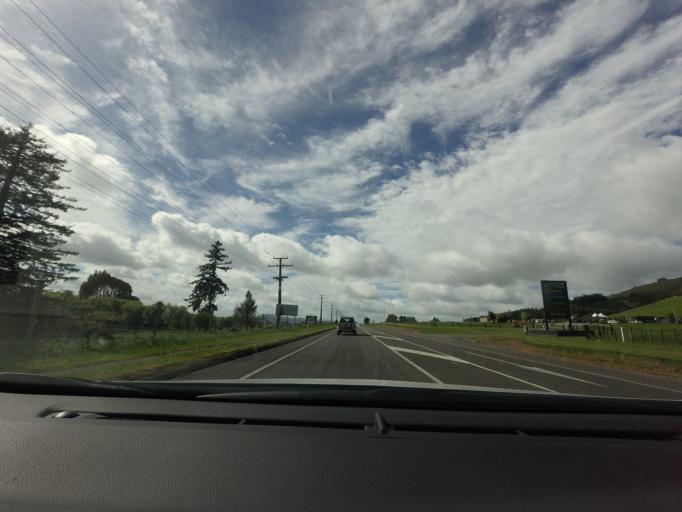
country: NZ
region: Bay of Plenty
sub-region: Rotorua District
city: Rotorua
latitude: -38.0973
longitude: 176.2192
